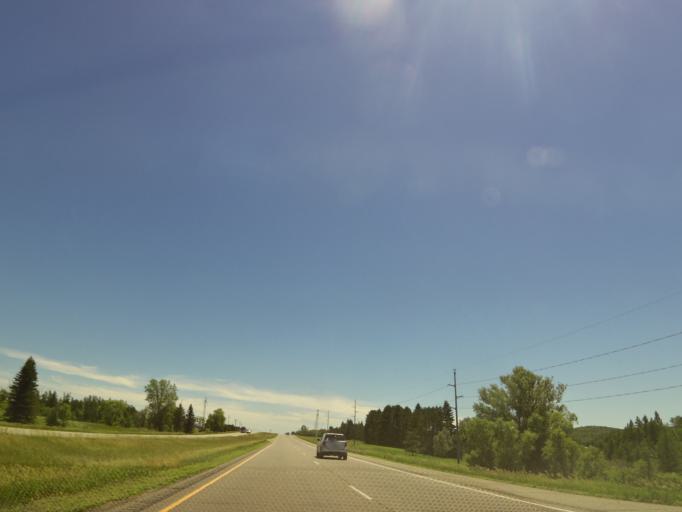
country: US
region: Minnesota
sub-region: Becker County
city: Frazee
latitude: 46.7636
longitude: -95.7782
